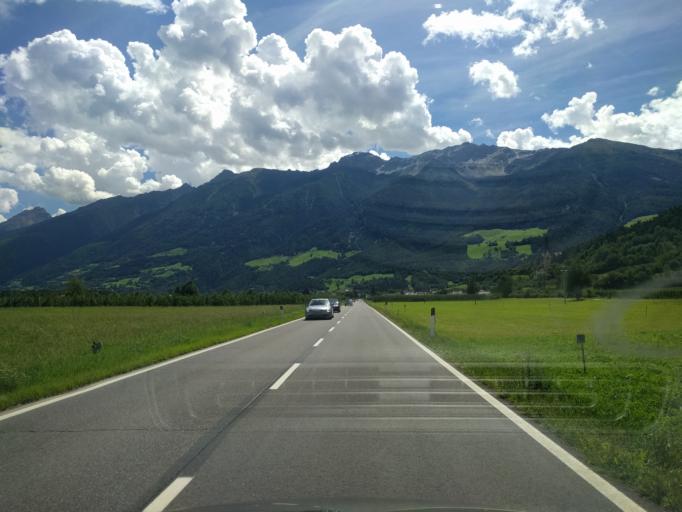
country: IT
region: Trentino-Alto Adige
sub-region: Bolzano
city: Prato Allo Stelvio
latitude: 46.6296
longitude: 10.5784
